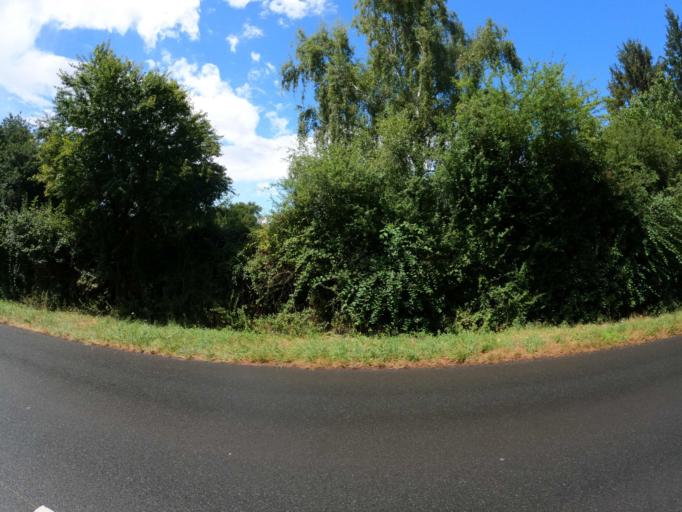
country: FR
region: Pays de la Loire
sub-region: Departement de Maine-et-Loire
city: Feneu
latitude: 47.5947
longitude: -0.5889
